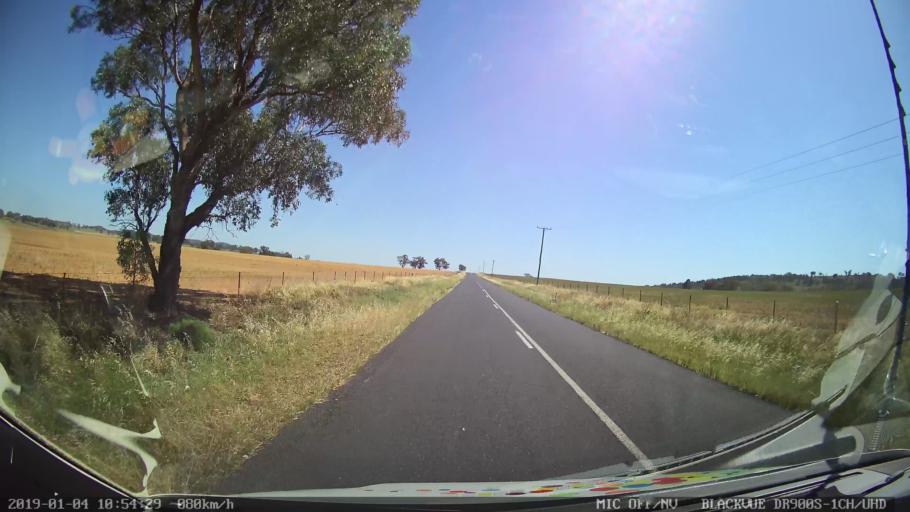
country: AU
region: New South Wales
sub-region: Cabonne
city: Molong
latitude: -33.2045
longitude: 148.6905
